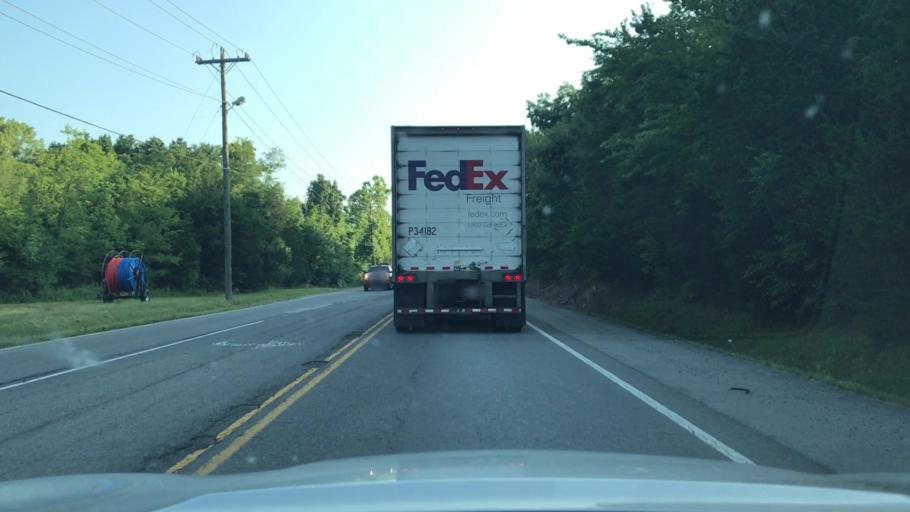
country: US
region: Tennessee
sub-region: Rutherford County
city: La Vergne
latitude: 36.0390
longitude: -86.6104
